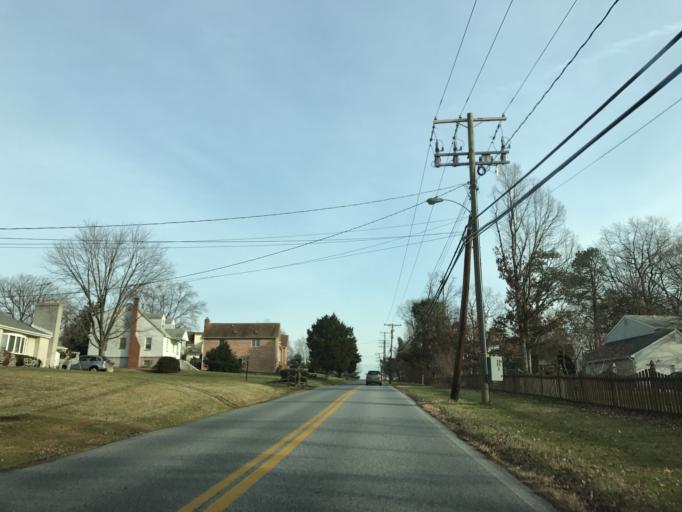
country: US
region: Maryland
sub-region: Baltimore County
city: White Marsh
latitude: 39.3841
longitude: -76.4538
